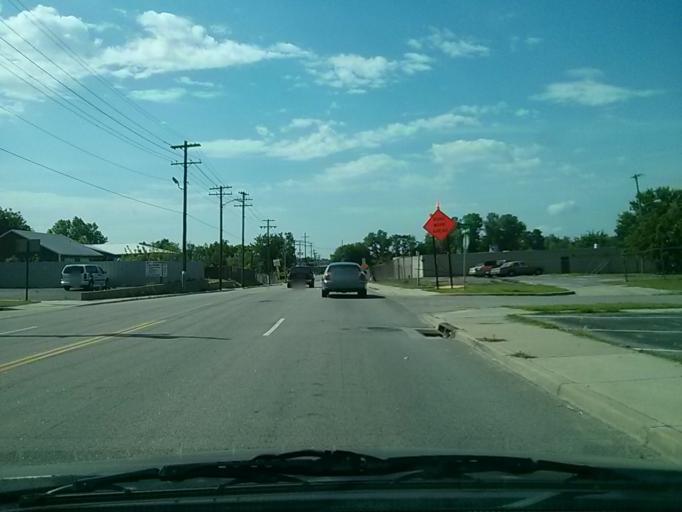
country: US
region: Oklahoma
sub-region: Tulsa County
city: Tulsa
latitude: 36.1645
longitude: -95.9756
